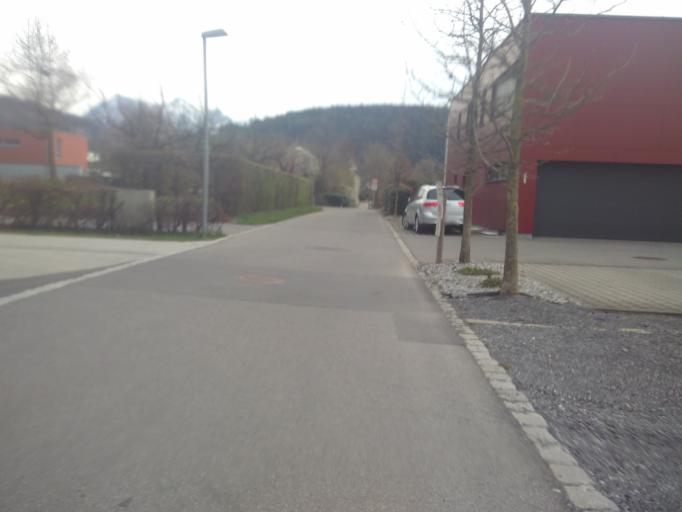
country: AT
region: Vorarlberg
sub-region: Politischer Bezirk Feldkirch
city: Feldkirch
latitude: 47.2644
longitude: 9.6102
